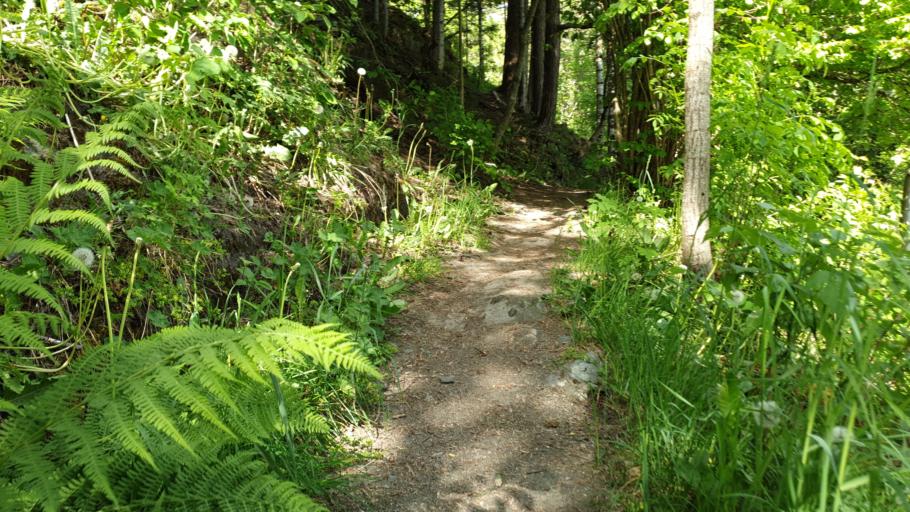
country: NO
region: Sor-Trondelag
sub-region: Rissa
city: Rissa
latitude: 63.5634
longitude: 9.9188
